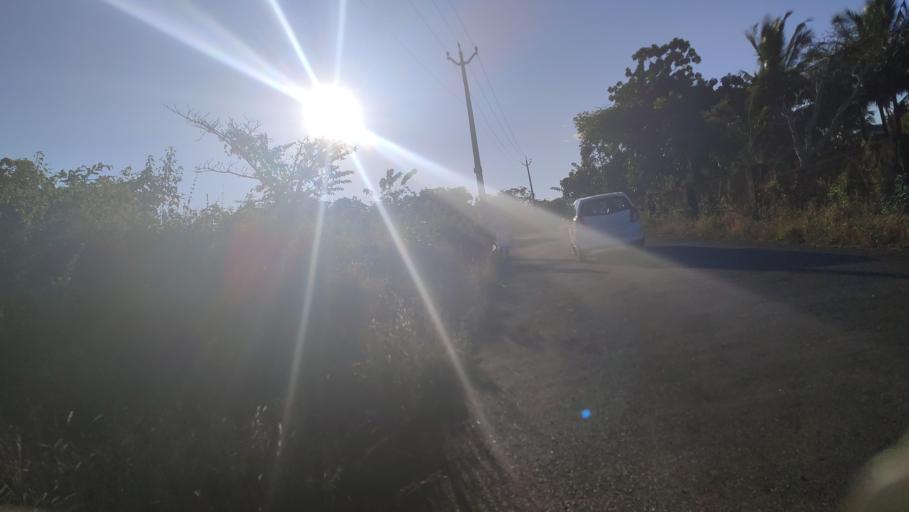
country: IN
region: Kerala
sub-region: Kasaragod District
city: Kasaragod
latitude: 12.4974
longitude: 75.0801
